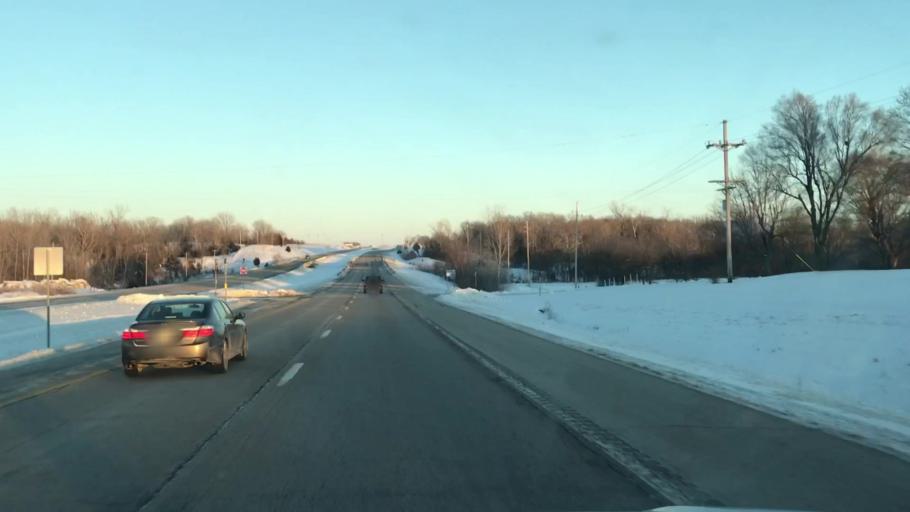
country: US
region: Missouri
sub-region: Clinton County
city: Cameron
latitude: 39.7547
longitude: -94.3198
